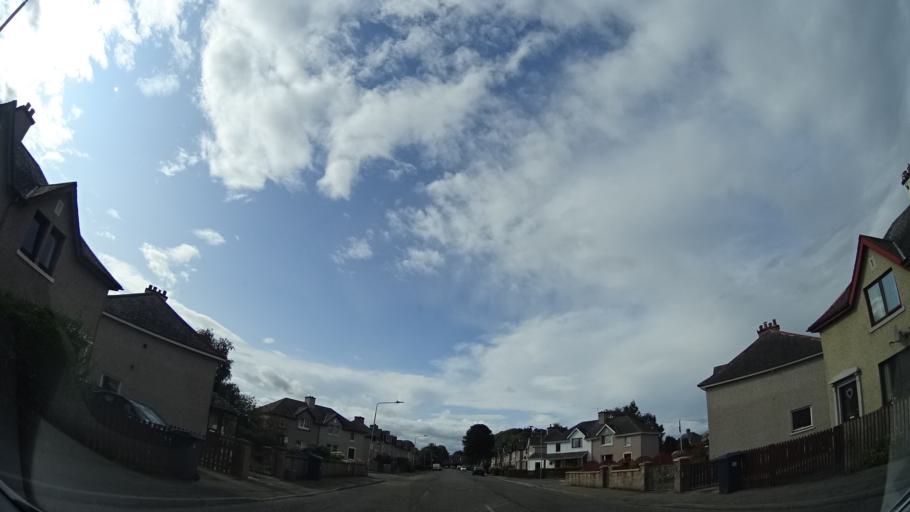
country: GB
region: Scotland
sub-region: Highland
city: Inverness
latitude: 57.4752
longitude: -4.2395
